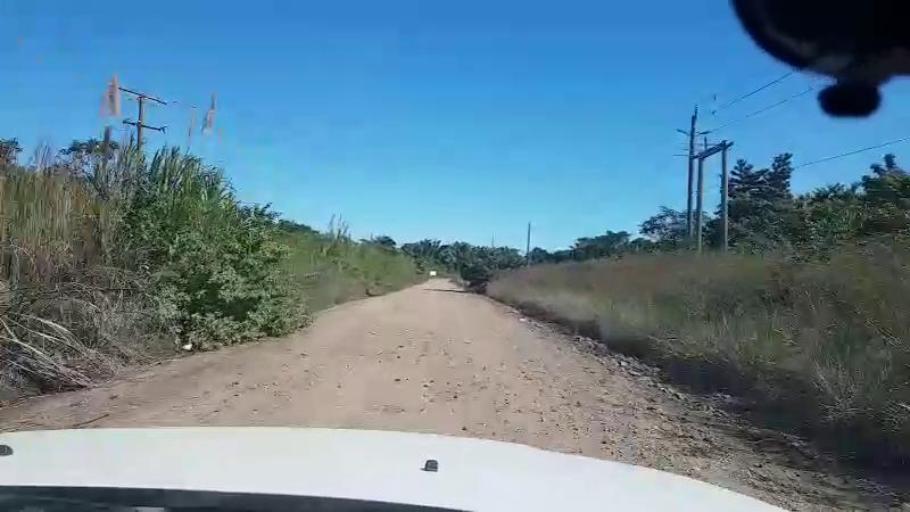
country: BZ
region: Stann Creek
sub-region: Dangriga
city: Dangriga
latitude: 17.1579
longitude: -88.3300
